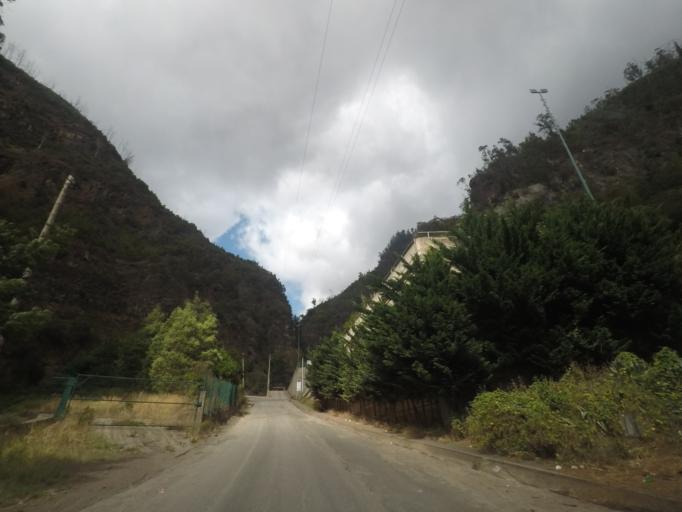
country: PT
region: Madeira
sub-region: Funchal
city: Nossa Senhora do Monte
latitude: 32.6838
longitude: -16.9151
